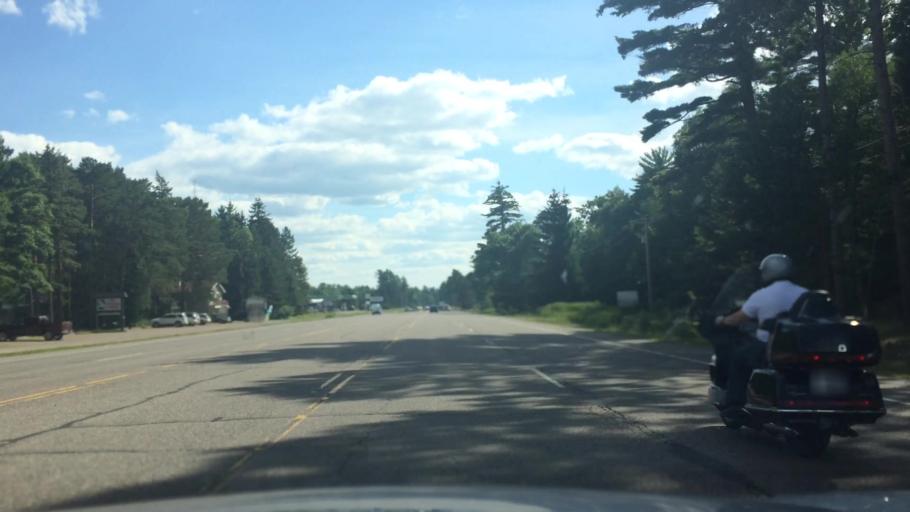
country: US
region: Wisconsin
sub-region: Vilas County
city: Lac du Flambeau
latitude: 45.8280
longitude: -89.7189
